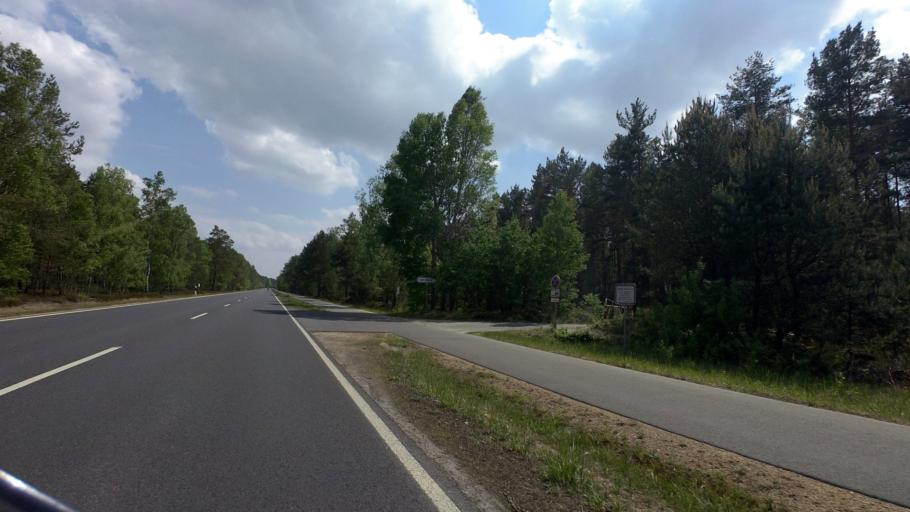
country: DE
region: Saxony
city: Rietschen
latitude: 51.4500
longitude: 14.7675
